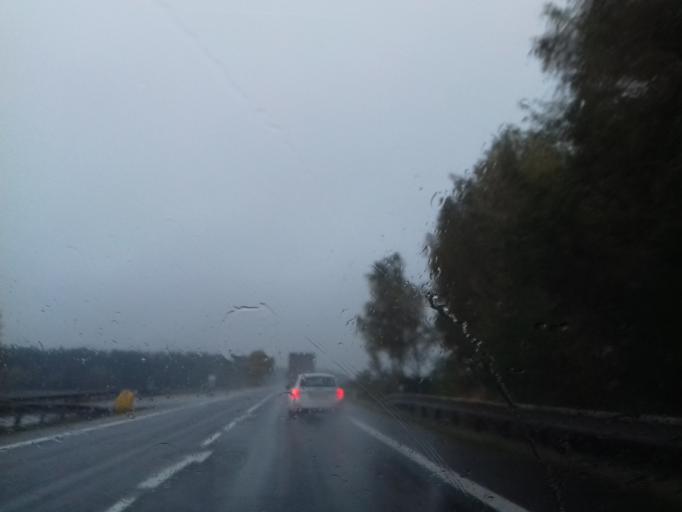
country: CZ
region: Pardubicky
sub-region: Okres Svitavy
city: Svitavy
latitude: 49.8146
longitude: 16.4163
